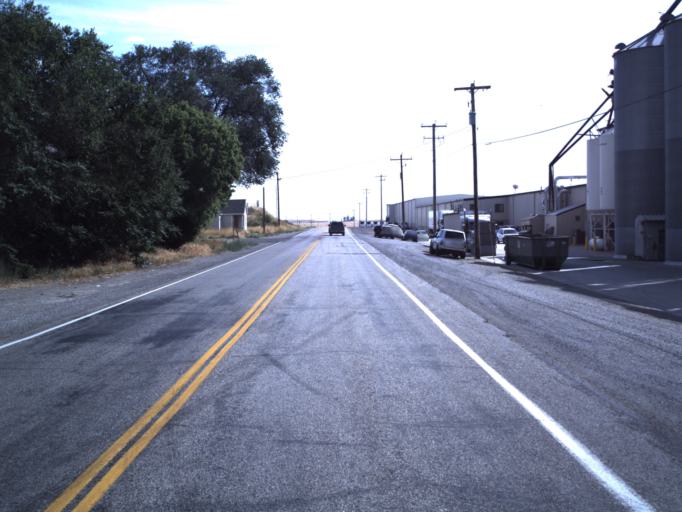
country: US
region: Utah
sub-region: Box Elder County
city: Garland
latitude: 41.7750
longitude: -112.0953
